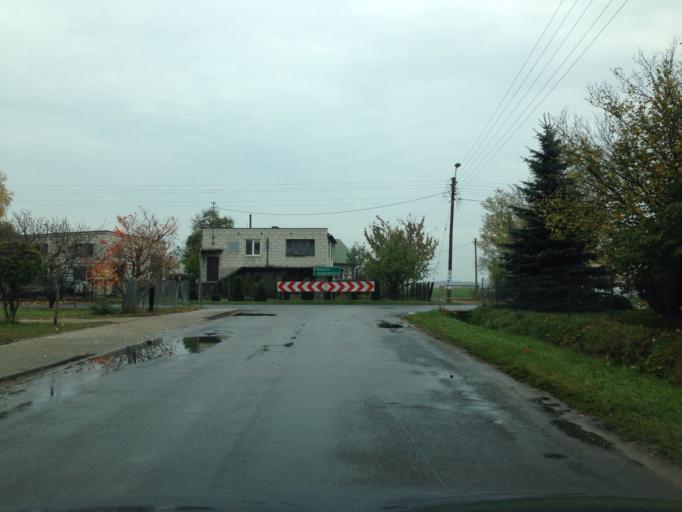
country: PL
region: Kujawsko-Pomorskie
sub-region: Powiat brodnicki
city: Swiedziebnia
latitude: 53.1633
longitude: 19.5256
